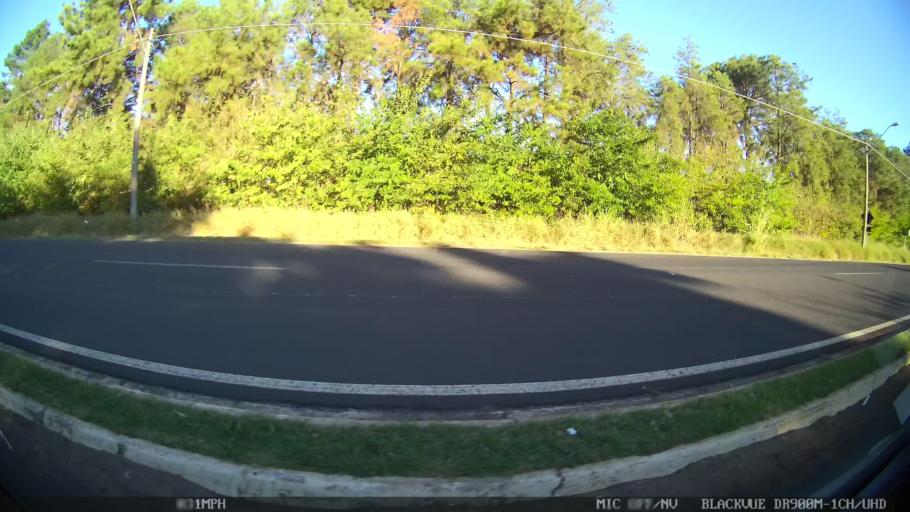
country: BR
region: Sao Paulo
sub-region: Americo Brasiliense
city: Americo Brasiliense
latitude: -21.7459
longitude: -48.1304
